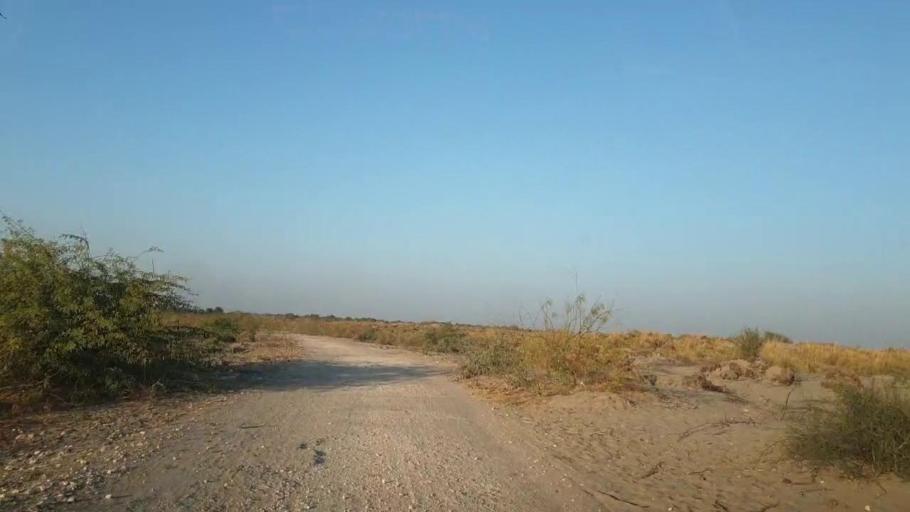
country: PK
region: Sindh
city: Mirpur Khas
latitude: 25.6823
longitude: 69.0499
